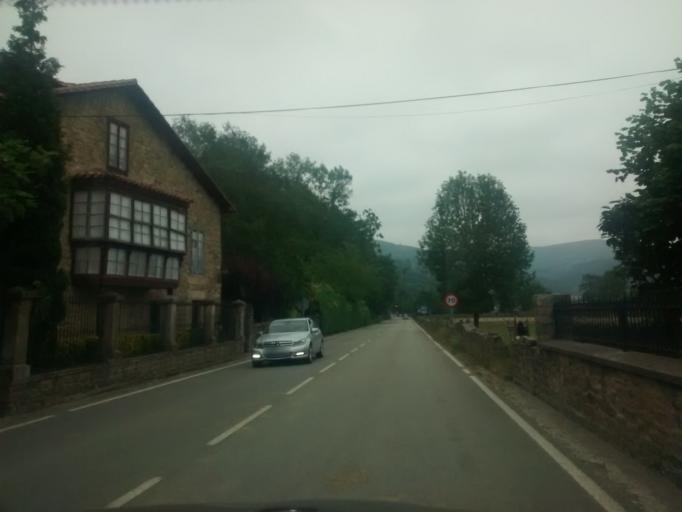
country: ES
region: Cantabria
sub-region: Provincia de Cantabria
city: Ruente
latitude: 43.2114
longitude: -4.3014
